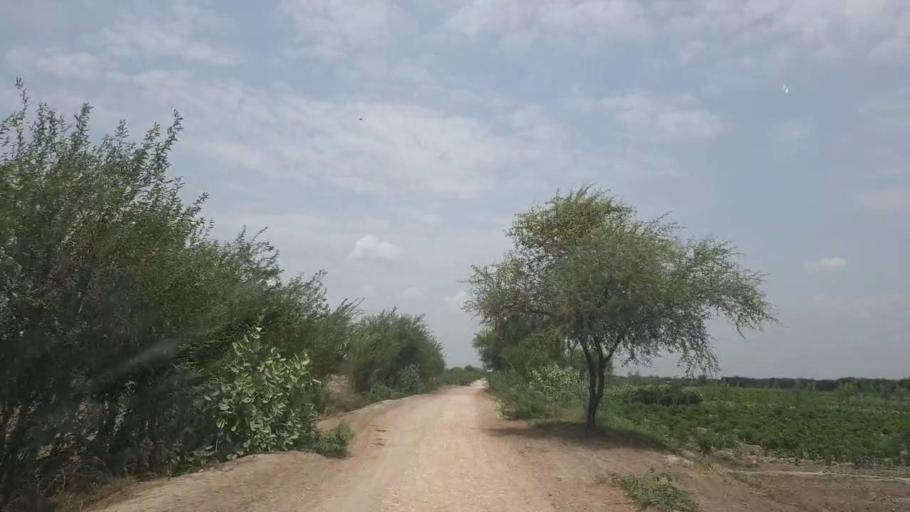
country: PK
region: Sindh
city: Naukot
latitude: 24.9359
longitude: 69.2007
